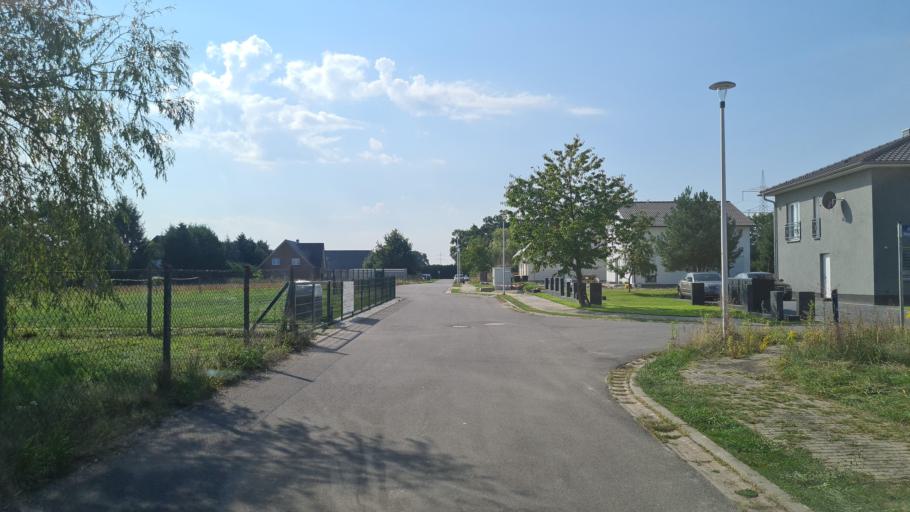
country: DE
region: Brandenburg
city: Werben
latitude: 51.7567
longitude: 14.1847
